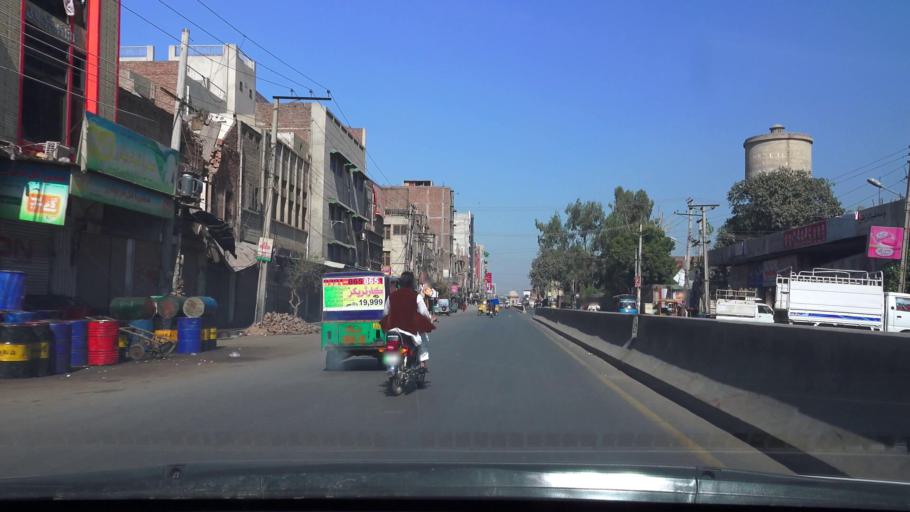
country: PK
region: Punjab
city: Faisalabad
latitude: 31.4157
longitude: 73.0806
